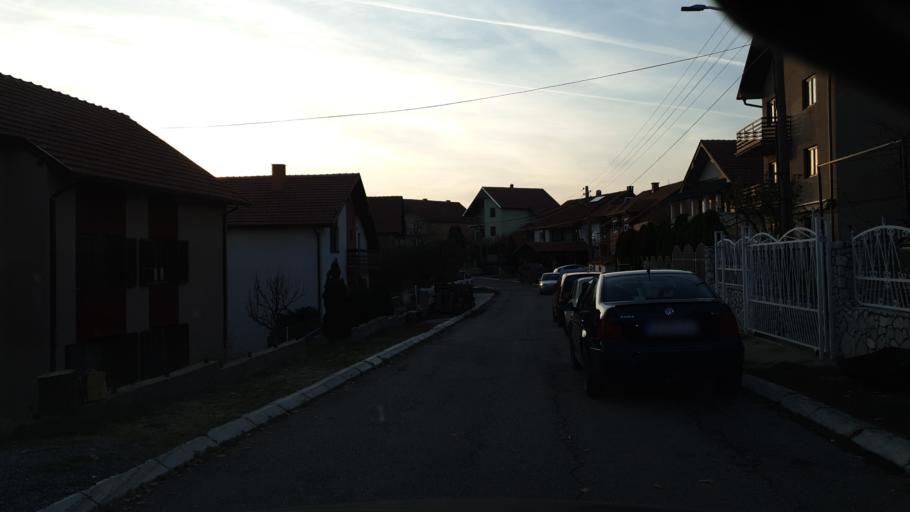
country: RS
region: Central Serbia
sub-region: Borski Okrug
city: Bor
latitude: 44.0585
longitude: 22.0862
